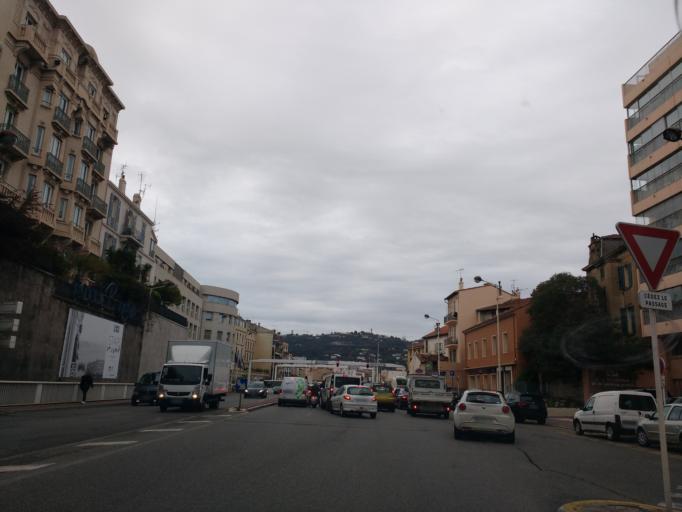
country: FR
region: Provence-Alpes-Cote d'Azur
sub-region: Departement des Alpes-Maritimes
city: Cannes
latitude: 43.5536
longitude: 7.0156
